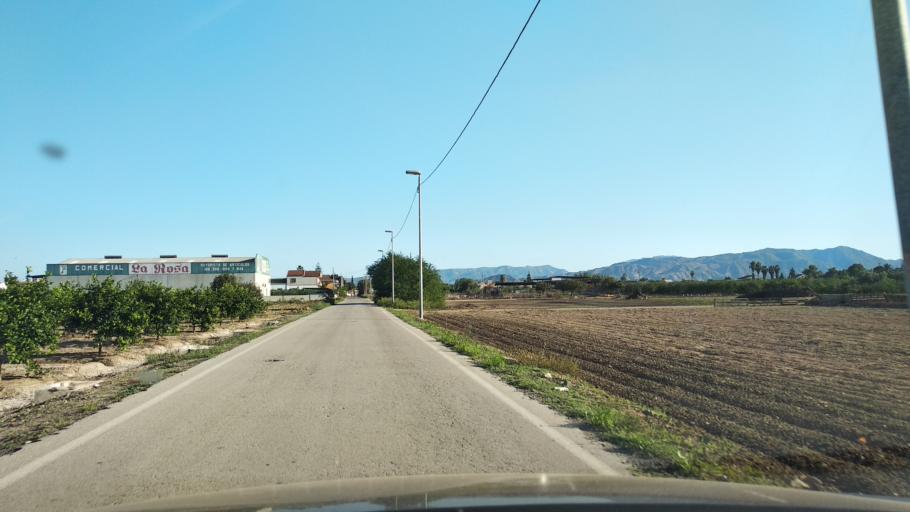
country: ES
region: Murcia
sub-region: Murcia
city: Santomera
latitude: 38.0430
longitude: -1.0357
